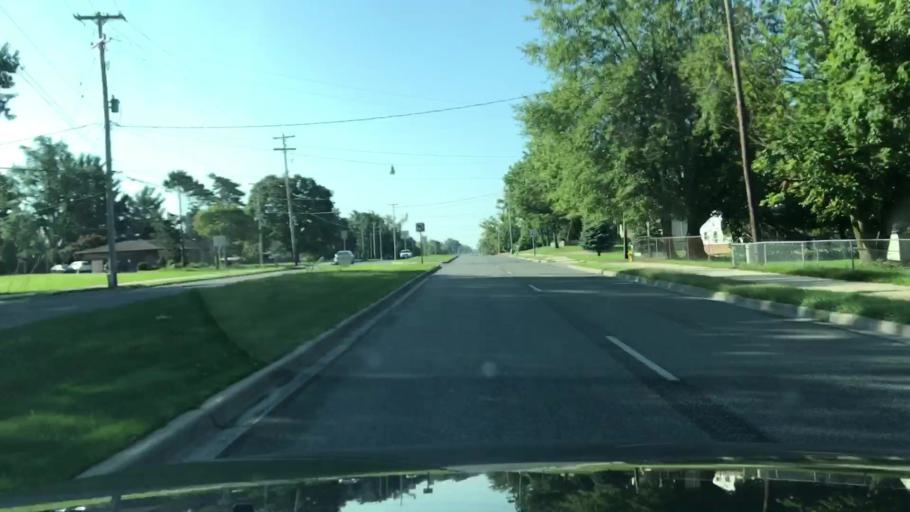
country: US
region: Michigan
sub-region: Kent County
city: Kentwood
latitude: 42.8763
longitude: -85.6257
